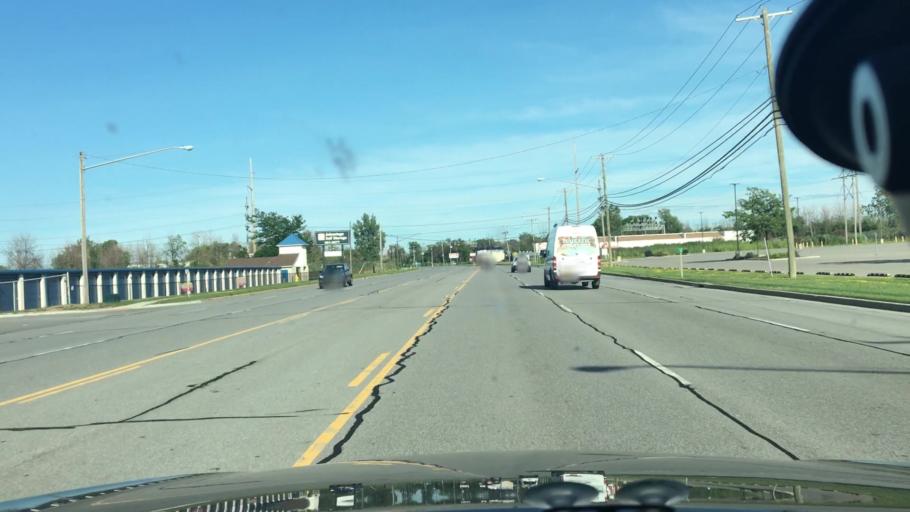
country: US
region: New York
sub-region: Erie County
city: Cheektowaga
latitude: 42.9093
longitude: -78.7267
